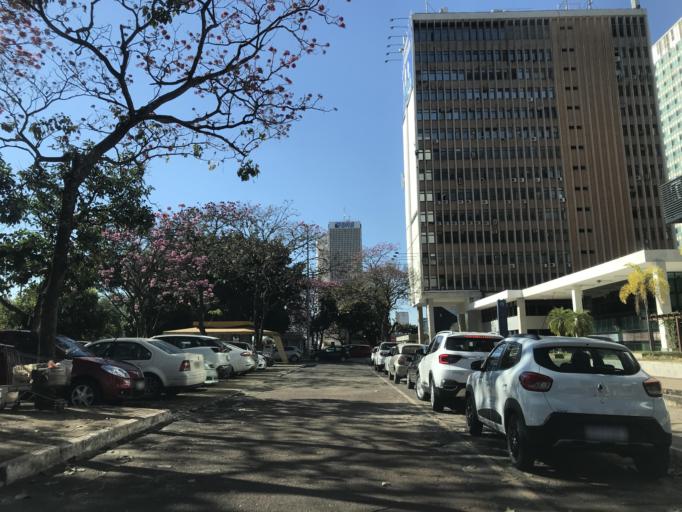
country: BR
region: Federal District
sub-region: Brasilia
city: Brasilia
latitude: -15.8005
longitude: -47.8839
